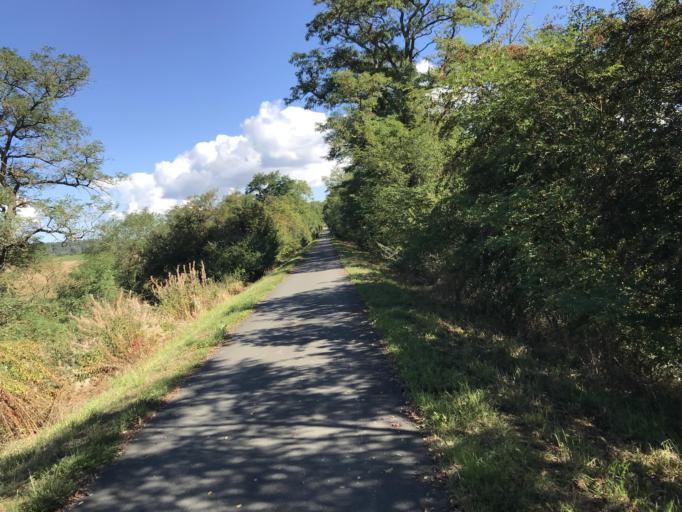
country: DE
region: Hesse
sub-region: Regierungsbezirk Kassel
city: Sachsenhausen
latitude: 51.2649
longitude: 8.9624
